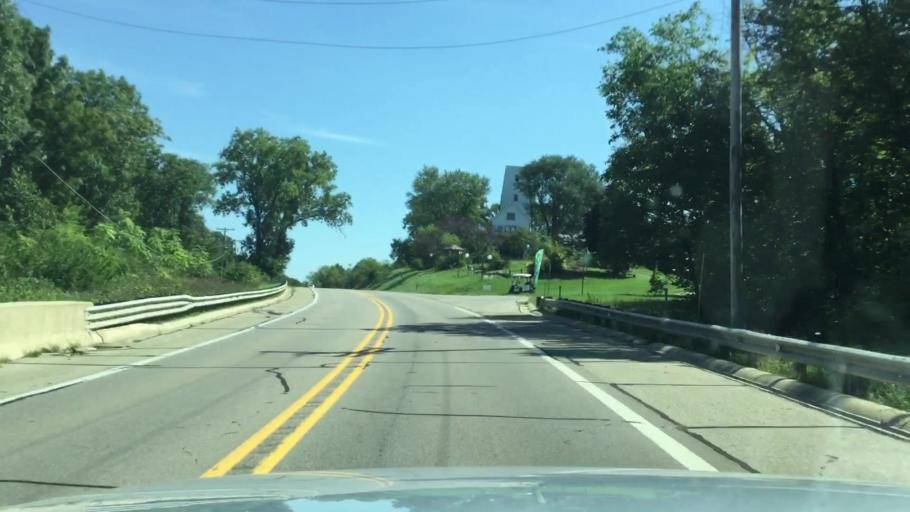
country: US
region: Michigan
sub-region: Jackson County
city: Brooklyn
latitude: 42.0561
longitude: -84.1586
